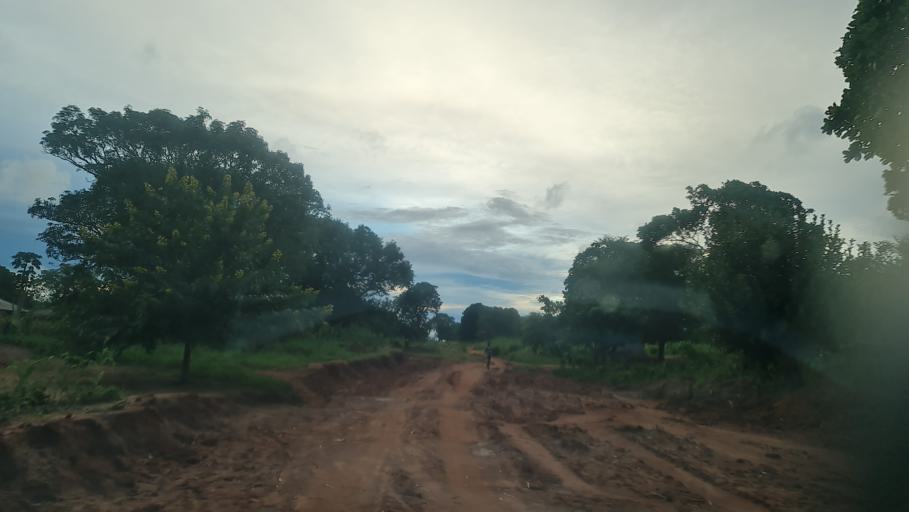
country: MZ
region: Nampula
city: Nacala
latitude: -14.7406
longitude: 39.9400
